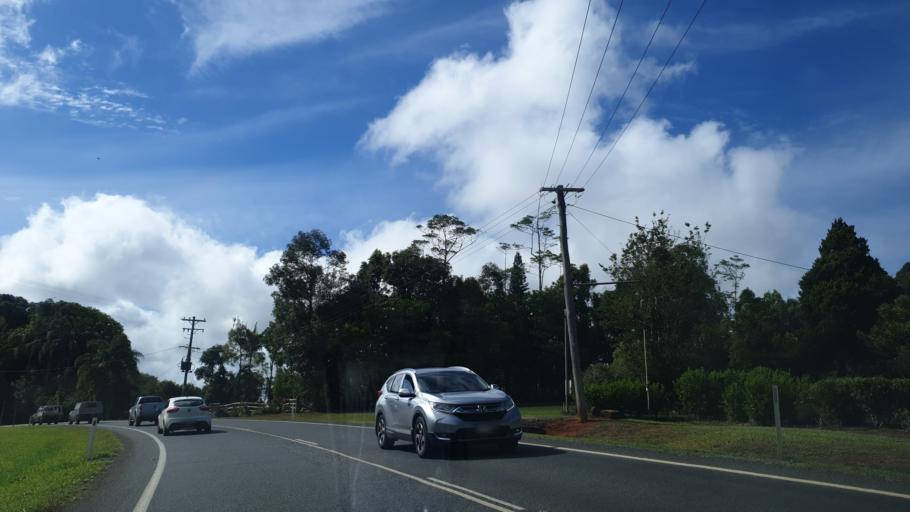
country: AU
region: Queensland
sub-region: Tablelands
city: Atherton
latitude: -17.3548
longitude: 145.5839
